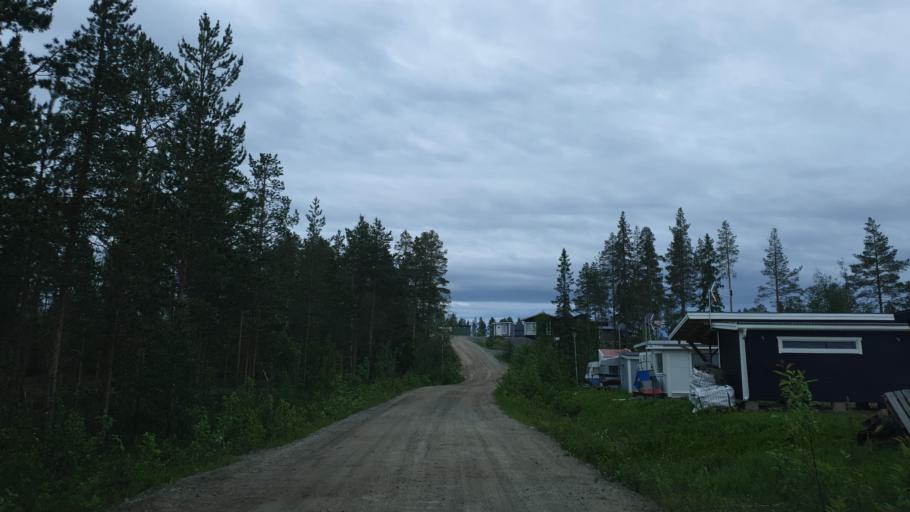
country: SE
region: Norrbotten
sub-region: Jokkmokks Kommun
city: Jokkmokk
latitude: 66.1540
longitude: 19.9909
